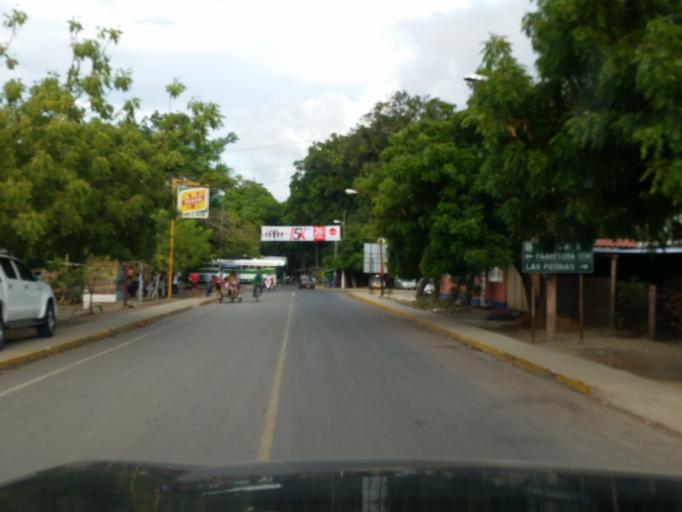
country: NI
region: Rivas
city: Rivas
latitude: 11.4399
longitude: -85.8369
